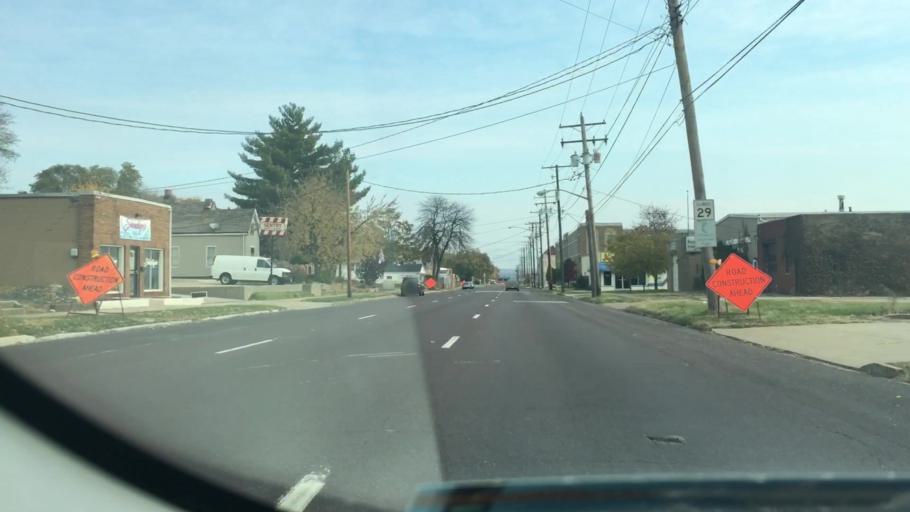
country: US
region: Illinois
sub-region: Peoria County
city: Peoria
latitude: 40.7011
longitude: -89.5750
